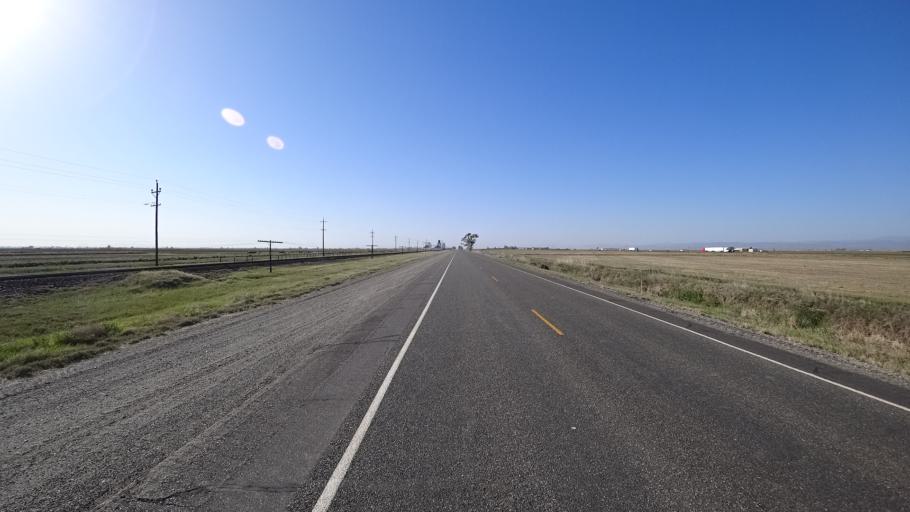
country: US
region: California
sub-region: Glenn County
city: Willows
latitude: 39.4787
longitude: -122.1931
